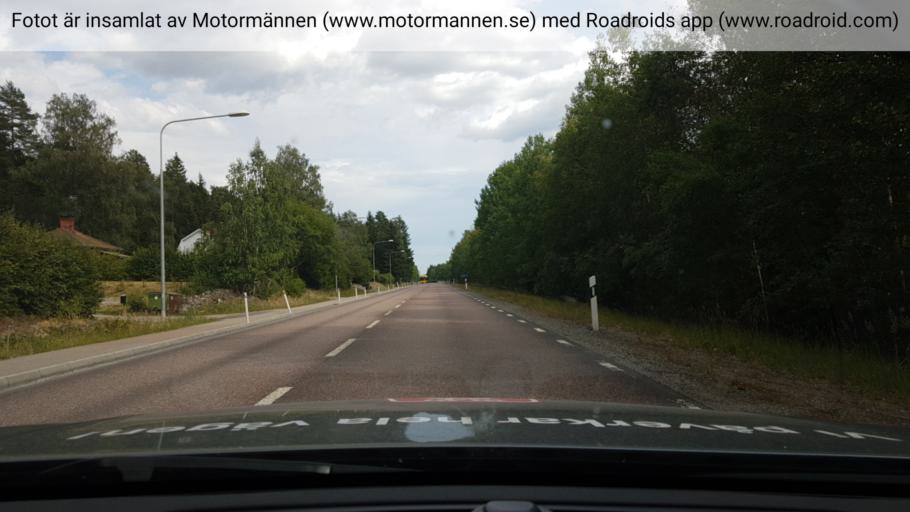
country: SE
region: Uppsala
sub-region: Enkopings Kommun
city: Orsundsbro
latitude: 59.8852
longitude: 17.2054
